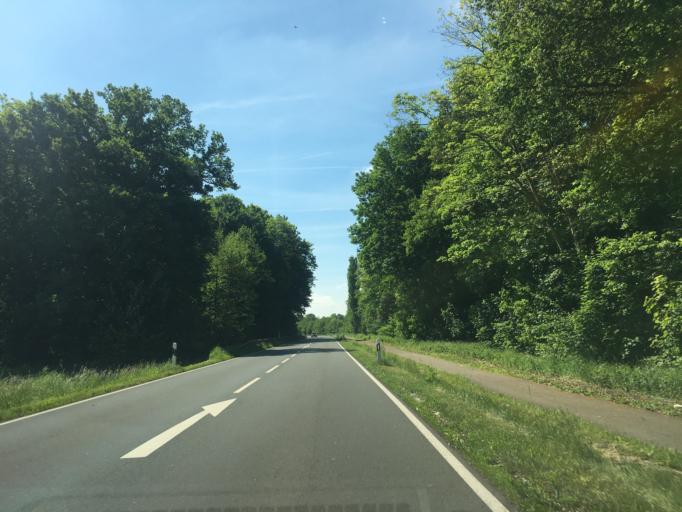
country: DE
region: North Rhine-Westphalia
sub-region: Regierungsbezirk Munster
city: Greven
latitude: 52.0559
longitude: 7.6138
